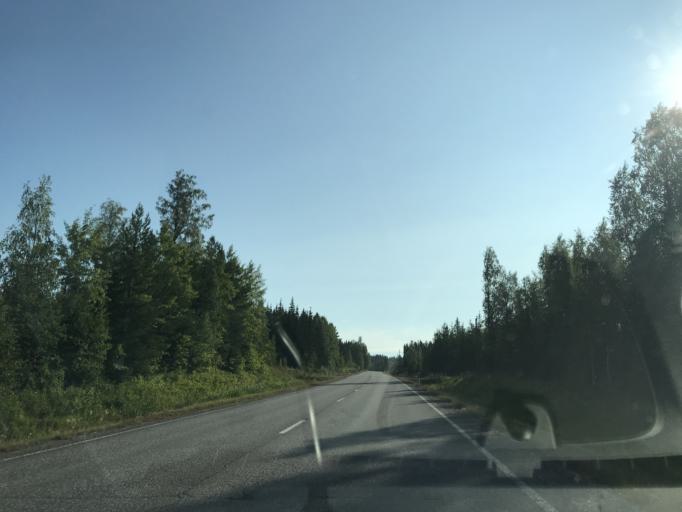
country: FI
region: Paijanne Tavastia
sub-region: Lahti
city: Orimattila
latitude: 60.7879
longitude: 25.6326
